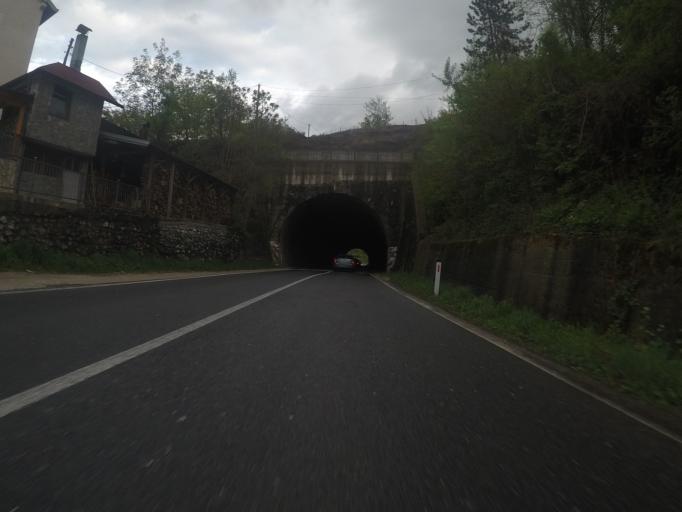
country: BA
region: Federation of Bosnia and Herzegovina
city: Konjic
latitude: 43.6855
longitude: 17.8905
